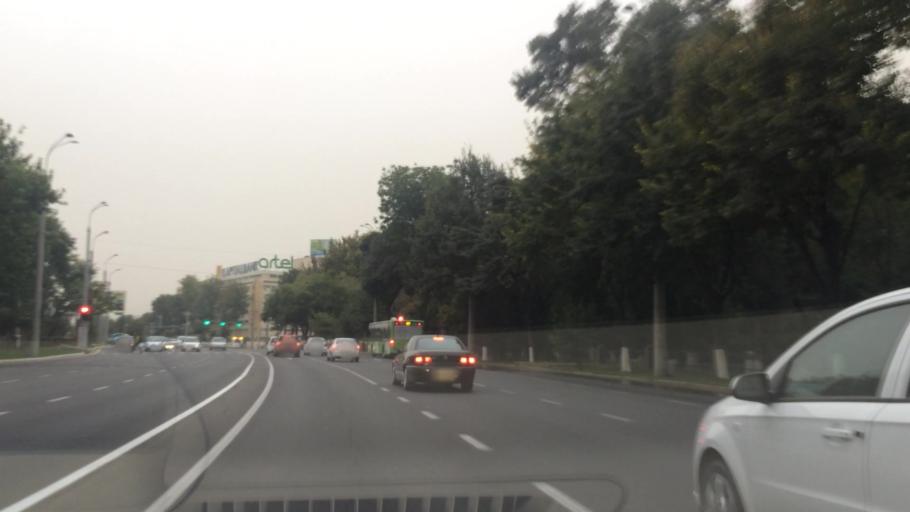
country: UZ
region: Toshkent Shahri
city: Tashkent
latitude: 41.3036
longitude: 69.2680
